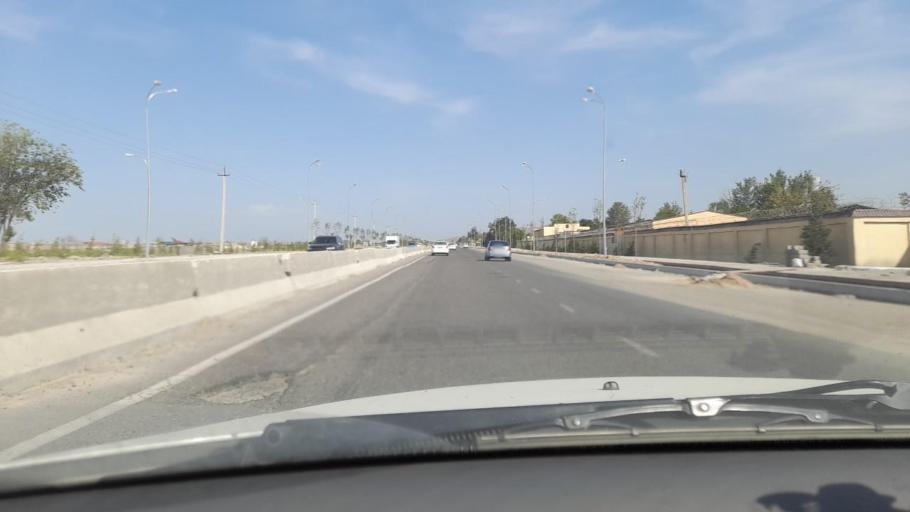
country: UZ
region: Samarqand
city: Samarqand
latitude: 39.7082
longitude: 66.9870
